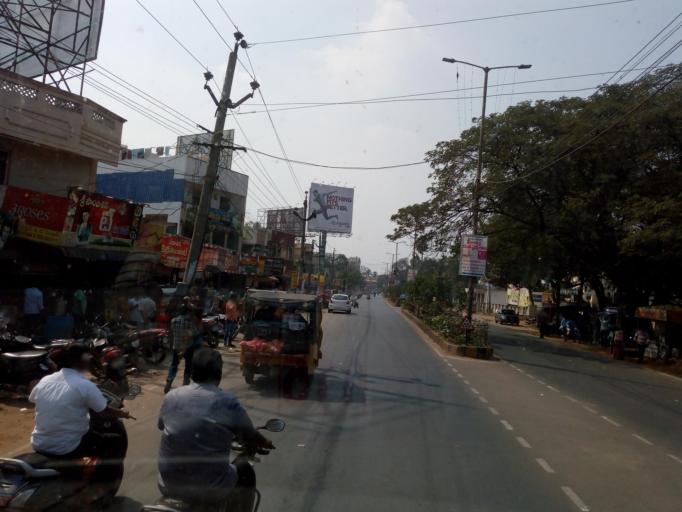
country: IN
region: Andhra Pradesh
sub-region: West Godavari
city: Eluru
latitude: 16.7093
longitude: 81.0916
